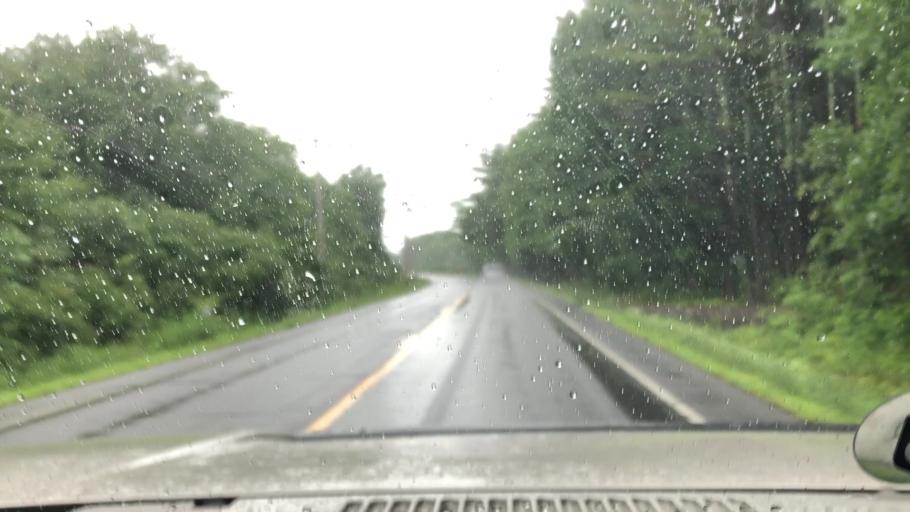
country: US
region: New York
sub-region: Greene County
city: Cairo
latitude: 42.2784
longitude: -73.9795
